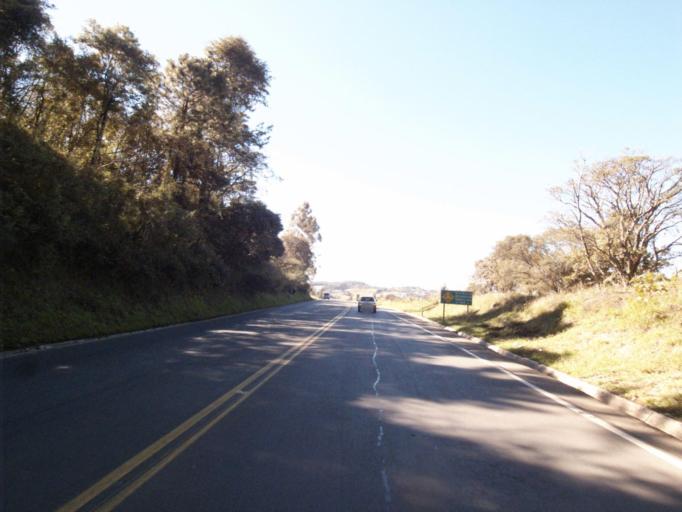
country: BR
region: Santa Catarina
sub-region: Chapeco
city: Chapeco
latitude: -26.9624
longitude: -52.5480
